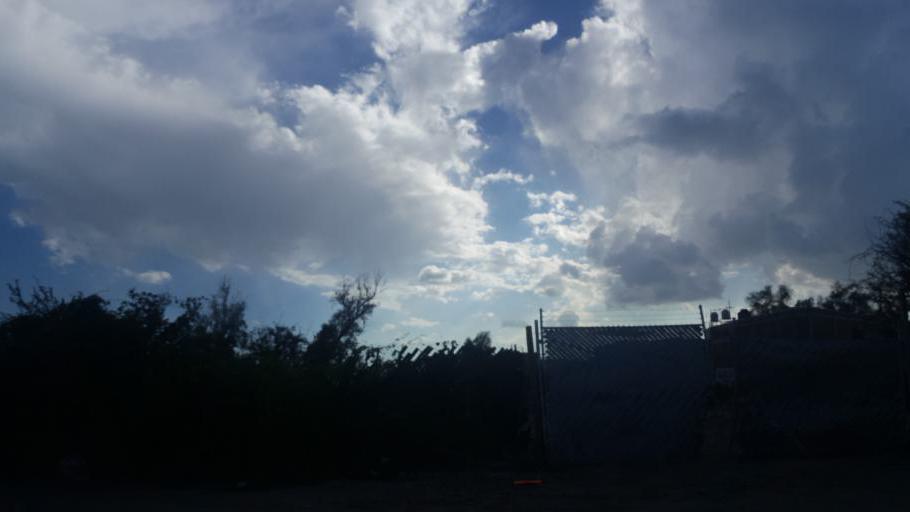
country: MX
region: Guanajuato
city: Leon
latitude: 21.0989
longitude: -101.7025
